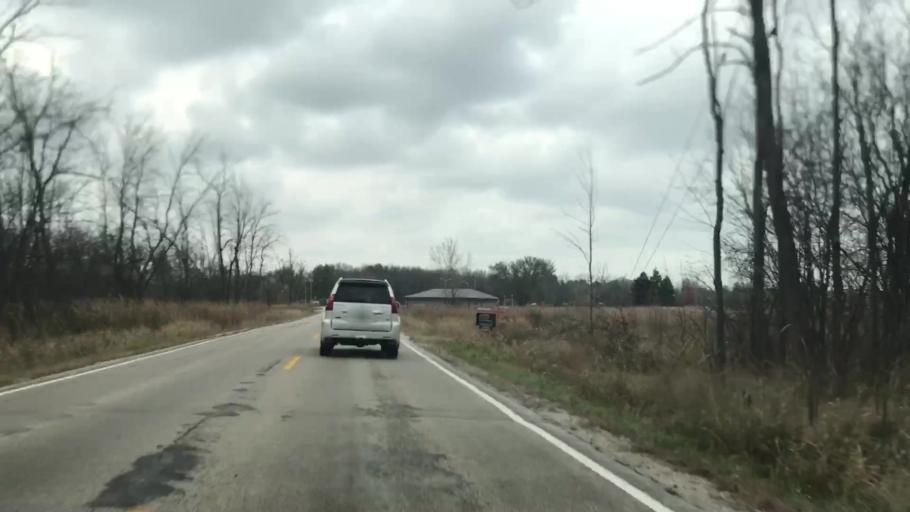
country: US
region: Wisconsin
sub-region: Waukesha County
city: Menomonee Falls
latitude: 43.1993
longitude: -88.1427
